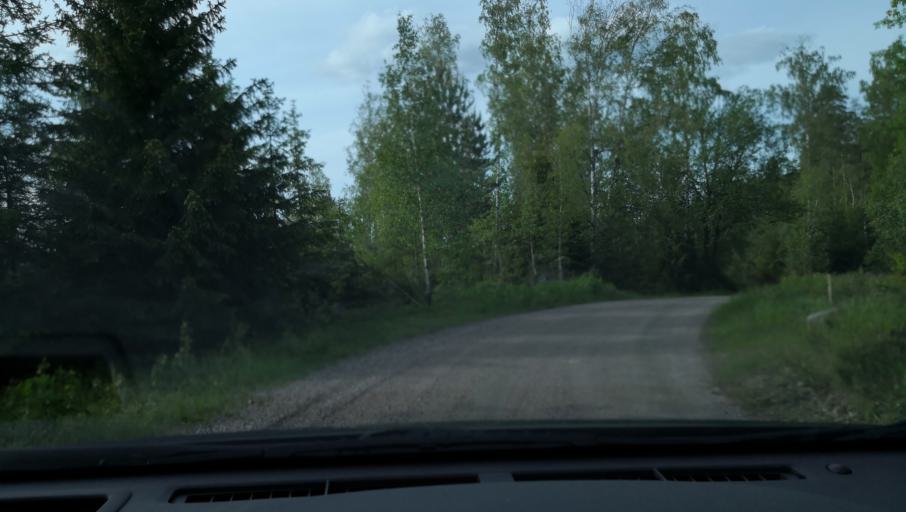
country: SE
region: Vaestmanland
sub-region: Arboga Kommun
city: Tyringe
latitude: 59.3647
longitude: 15.9928
